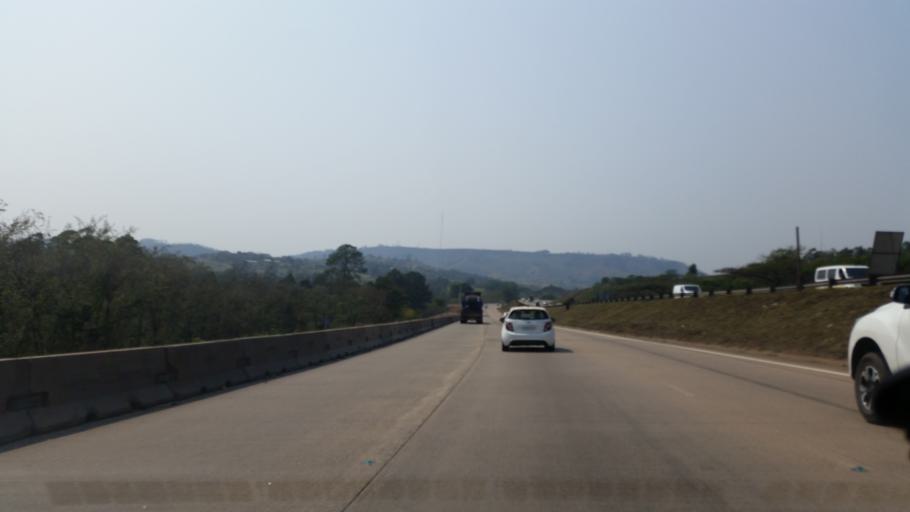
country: ZA
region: KwaZulu-Natal
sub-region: eThekwini Metropolitan Municipality
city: Mpumalanga
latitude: -29.7623
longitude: 30.6743
